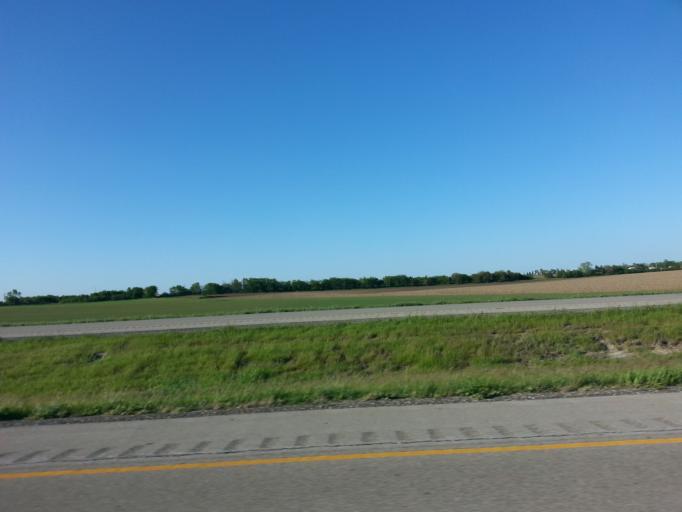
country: US
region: Illinois
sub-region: McLean County
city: Le Roy
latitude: 40.3479
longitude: -88.7851
